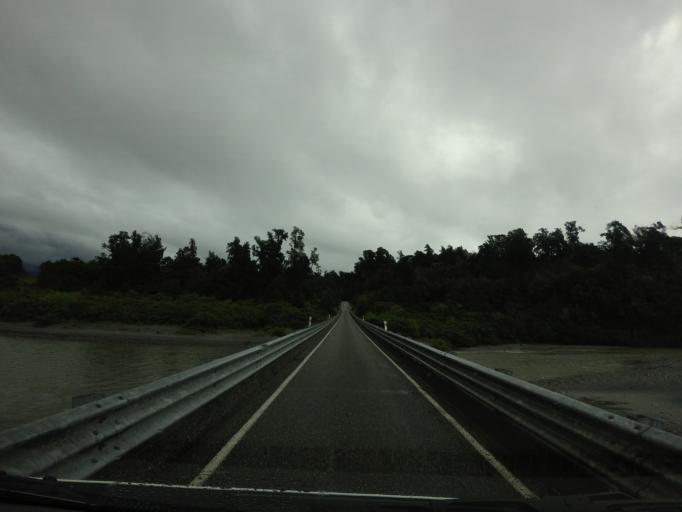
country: NZ
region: West Coast
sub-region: Westland District
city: Hokitika
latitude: -42.9804
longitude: 170.6851
